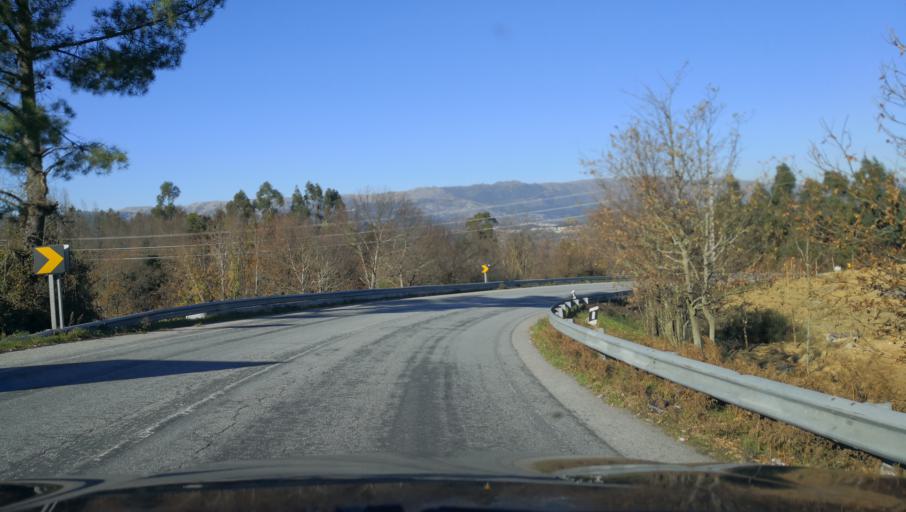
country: PT
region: Viseu
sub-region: Vouzela
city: Vouzela
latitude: 40.7225
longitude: -8.1332
